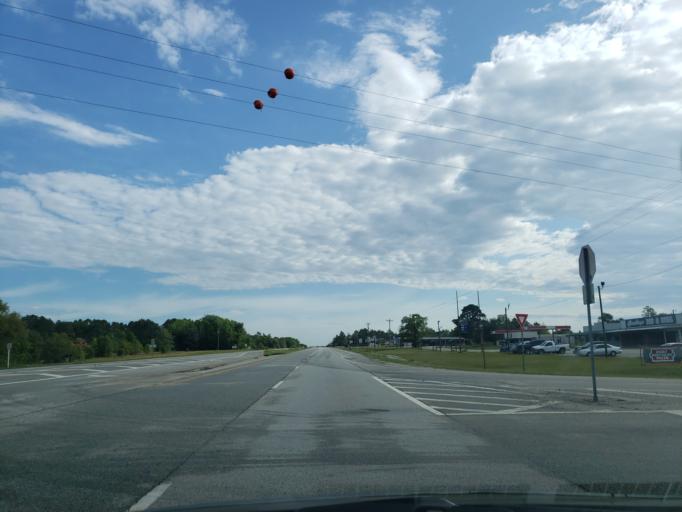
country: US
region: Georgia
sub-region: Emanuel County
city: Swainsboro
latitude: 32.4034
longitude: -82.3061
